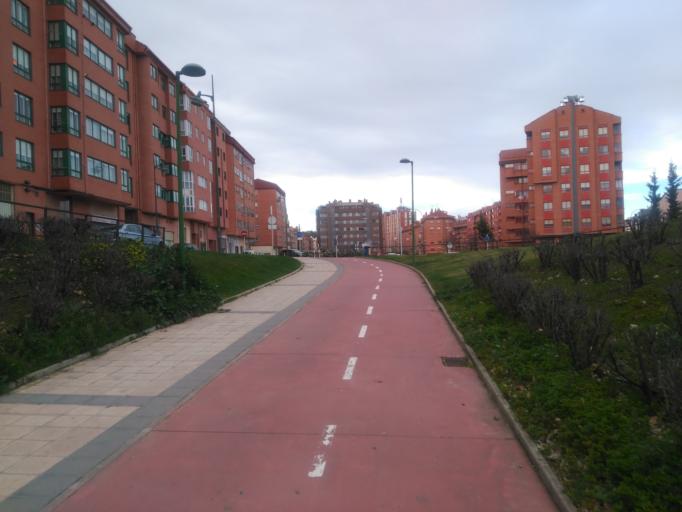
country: ES
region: Castille and Leon
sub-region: Provincia de Burgos
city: Burgos
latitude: 42.3286
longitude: -3.7006
